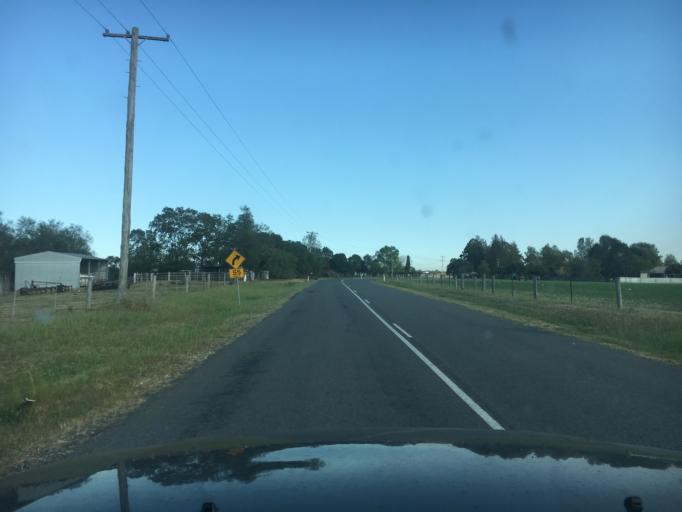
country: AU
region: New South Wales
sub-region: Cessnock
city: Branxton
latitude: -32.6033
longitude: 151.3398
